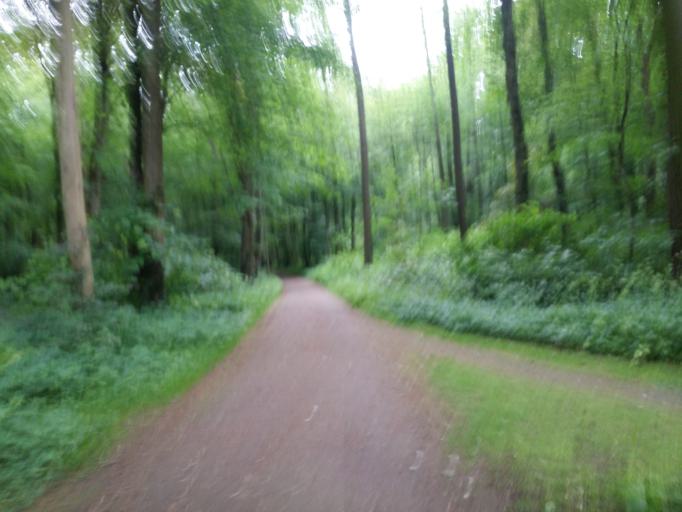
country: DE
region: Lower Saxony
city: Rastede
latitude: 53.2391
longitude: 8.2233
